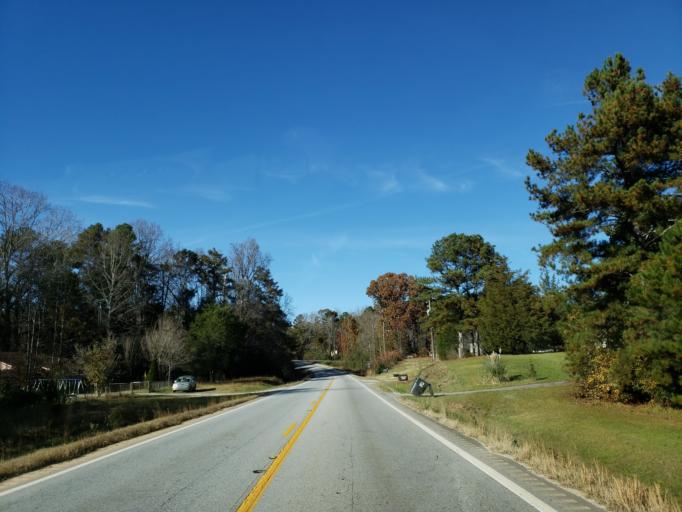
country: US
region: Alabama
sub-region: Calhoun County
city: Choccolocco
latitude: 33.5693
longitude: -85.6658
